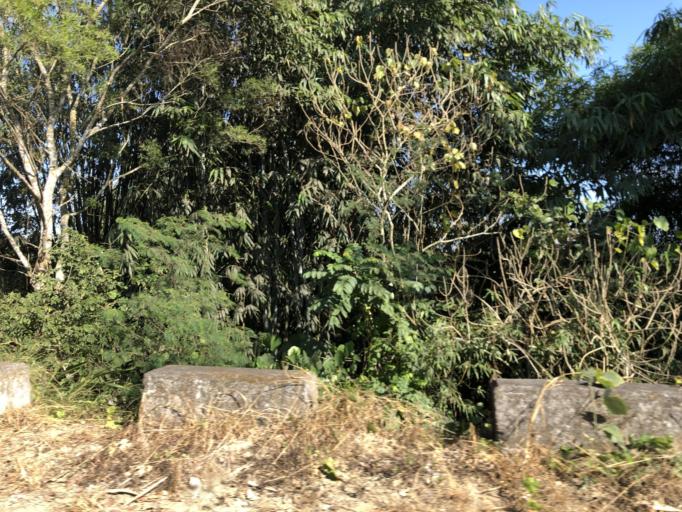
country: TW
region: Taiwan
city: Yujing
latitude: 23.0293
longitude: 120.3856
